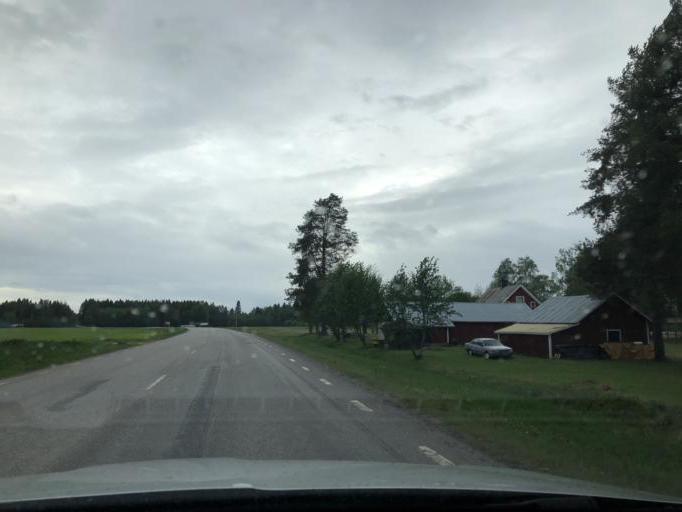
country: SE
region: Norrbotten
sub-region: Pitea Kommun
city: Roknas
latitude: 65.3751
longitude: 21.2807
